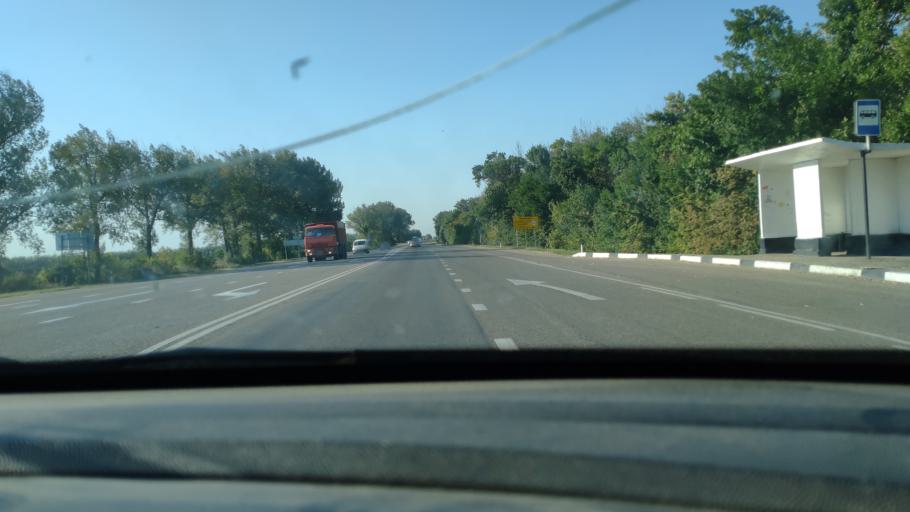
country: RU
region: Krasnodarskiy
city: Medvedovskaya
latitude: 45.4537
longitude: 38.9898
